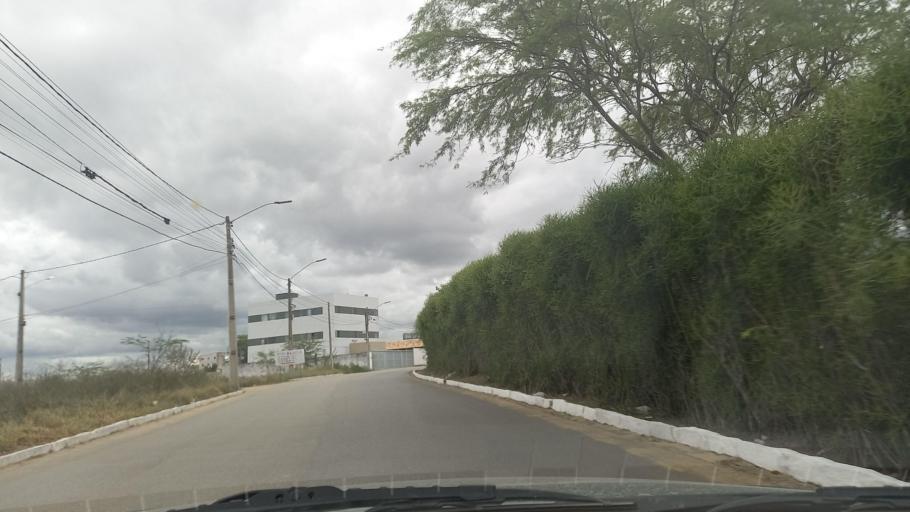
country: BR
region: Pernambuco
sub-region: Caruaru
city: Caruaru
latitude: -8.2567
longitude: -35.9657
